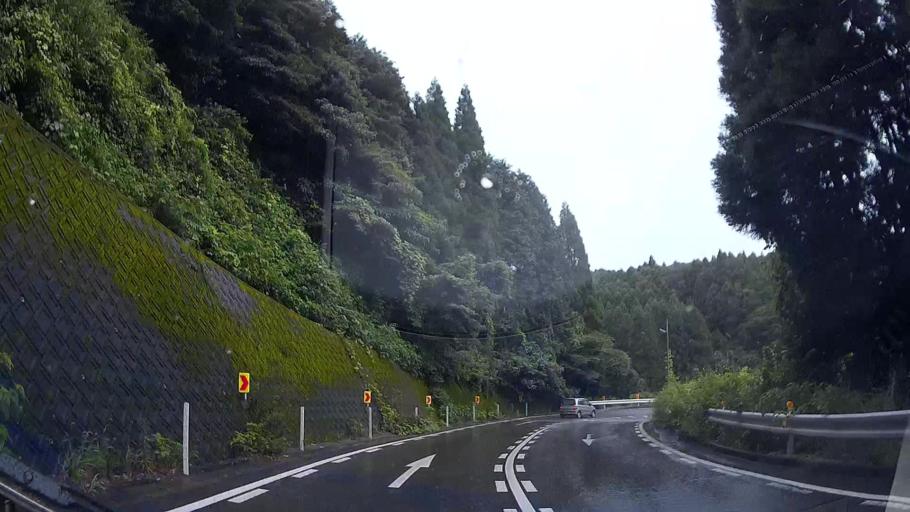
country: JP
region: Kumamoto
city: Aso
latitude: 32.8693
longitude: 130.9966
